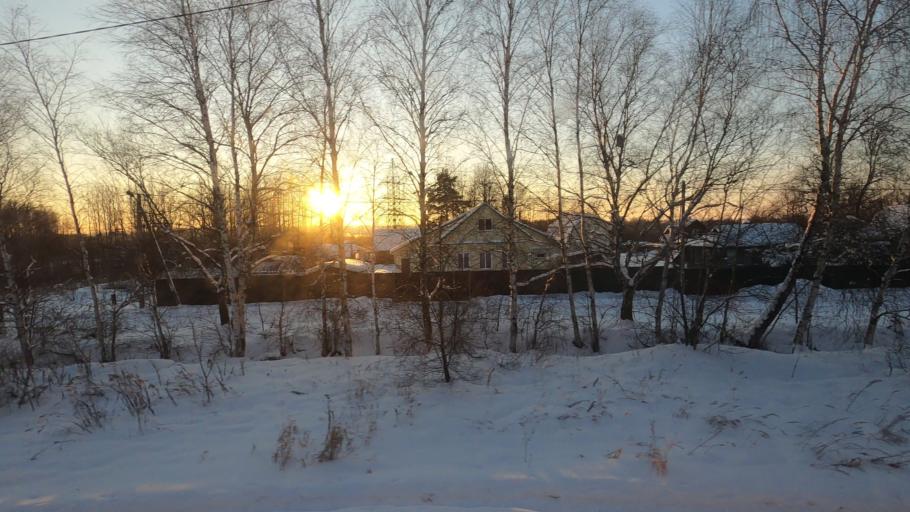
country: RU
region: Moskovskaya
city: Dmitrov
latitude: 56.3814
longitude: 37.5178
